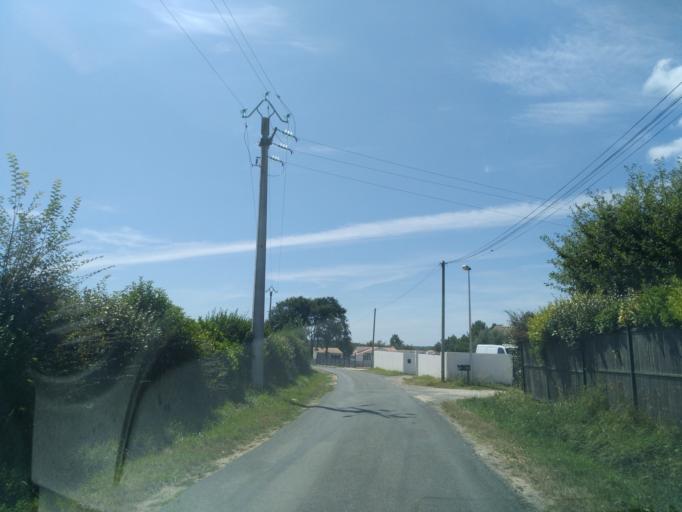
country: FR
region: Poitou-Charentes
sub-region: Departement de la Charente-Maritime
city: Breuillet
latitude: 45.7001
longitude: -1.0687
